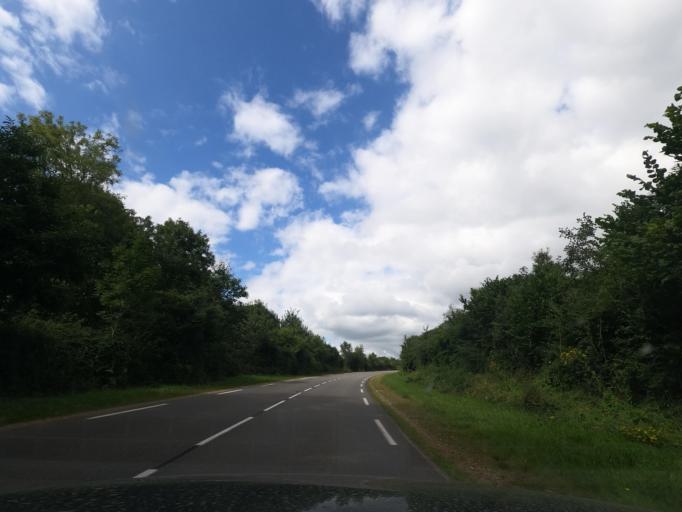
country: FR
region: Lower Normandy
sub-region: Departement de l'Orne
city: Champsecret
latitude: 48.6388
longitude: -0.5499
